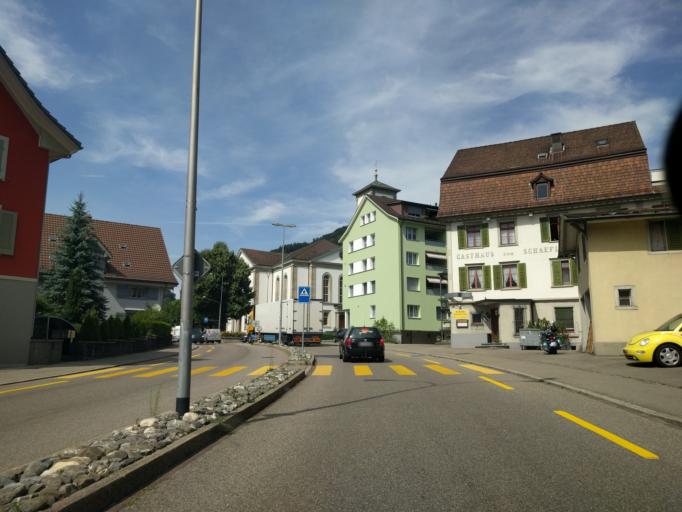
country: CH
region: Saint Gallen
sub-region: Wahlkreis Toggenburg
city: Wattwil
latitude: 47.3032
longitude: 9.0882
